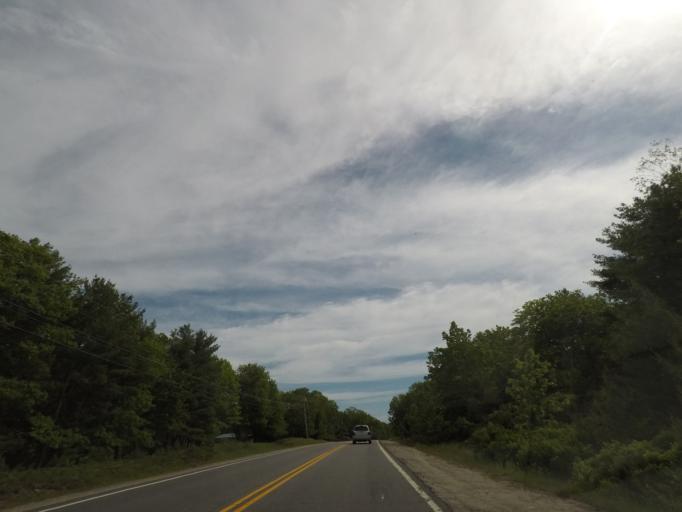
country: US
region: Maine
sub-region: Sagadahoc County
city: Richmond
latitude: 44.1099
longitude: -69.7817
